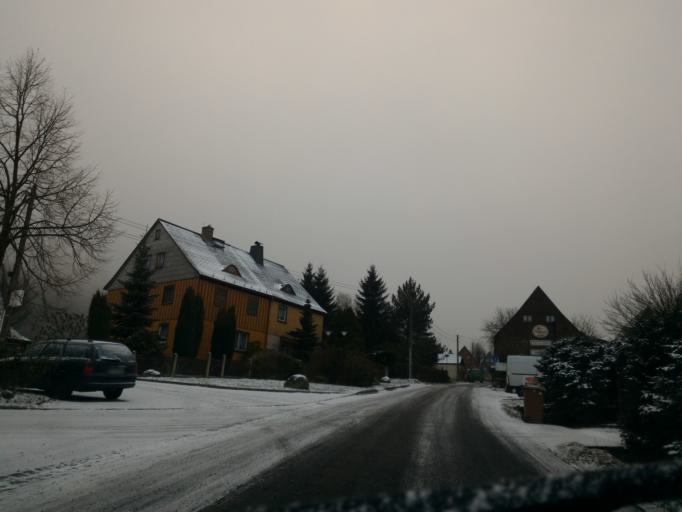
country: DE
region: Saxony
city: Grossschonau
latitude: 50.8585
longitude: 14.6545
